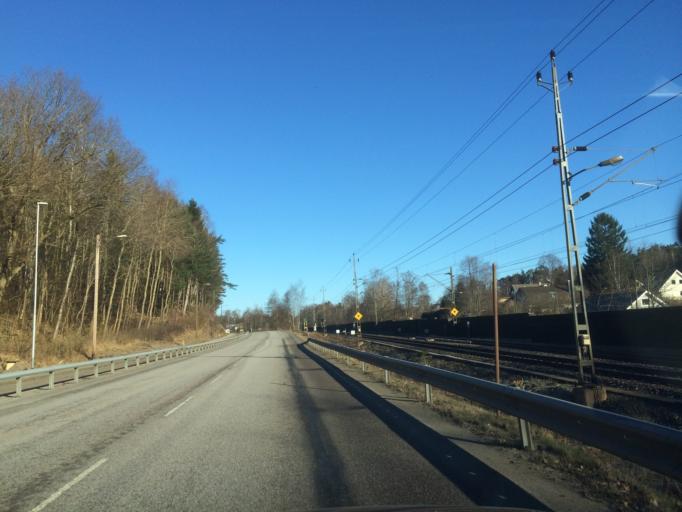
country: SE
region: Vaestra Goetaland
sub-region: Molndal
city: Lindome
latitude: 57.5832
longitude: 12.0742
